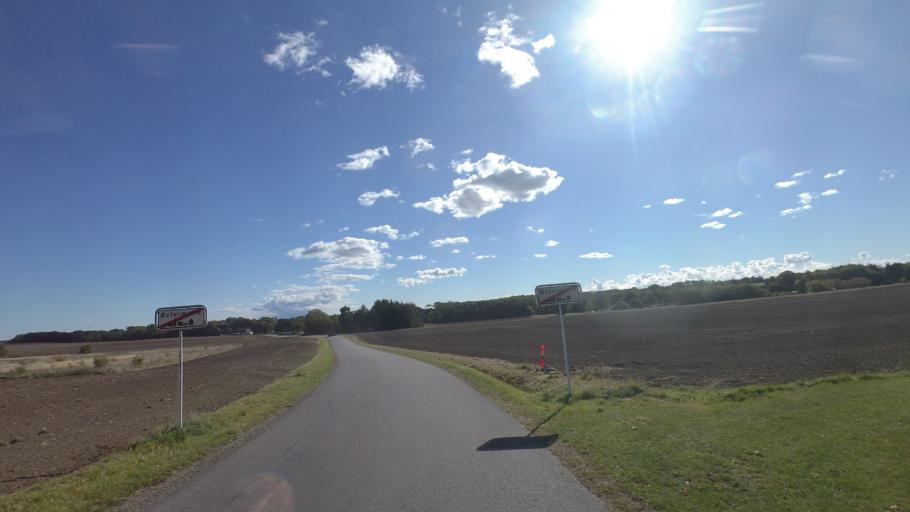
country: DK
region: Capital Region
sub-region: Bornholm Kommune
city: Akirkeby
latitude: 55.1371
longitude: 15.0173
